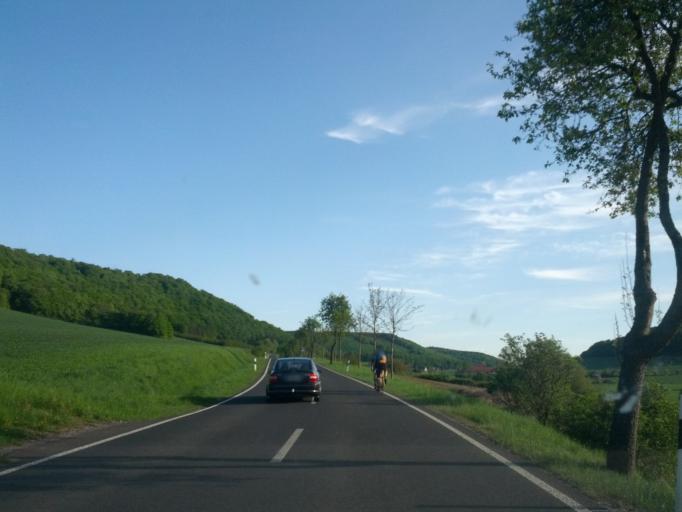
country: DE
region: Thuringia
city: Ifta
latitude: 51.0936
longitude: 10.2160
